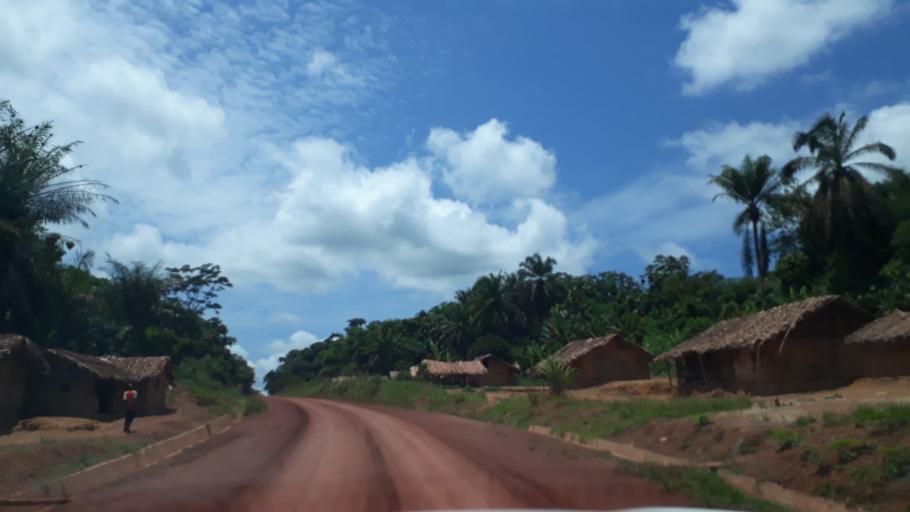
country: CD
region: Eastern Province
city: Kisangani
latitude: 0.5176
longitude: 25.8087
